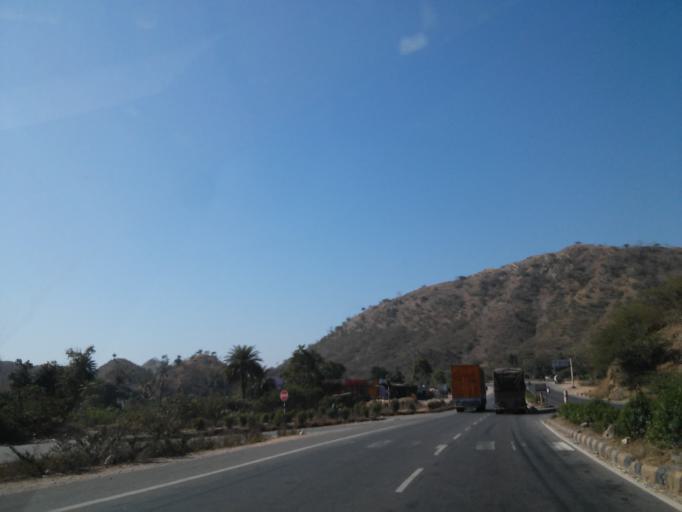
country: IN
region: Rajasthan
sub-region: Udaipur
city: Salumbar
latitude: 24.1946
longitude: 73.7023
